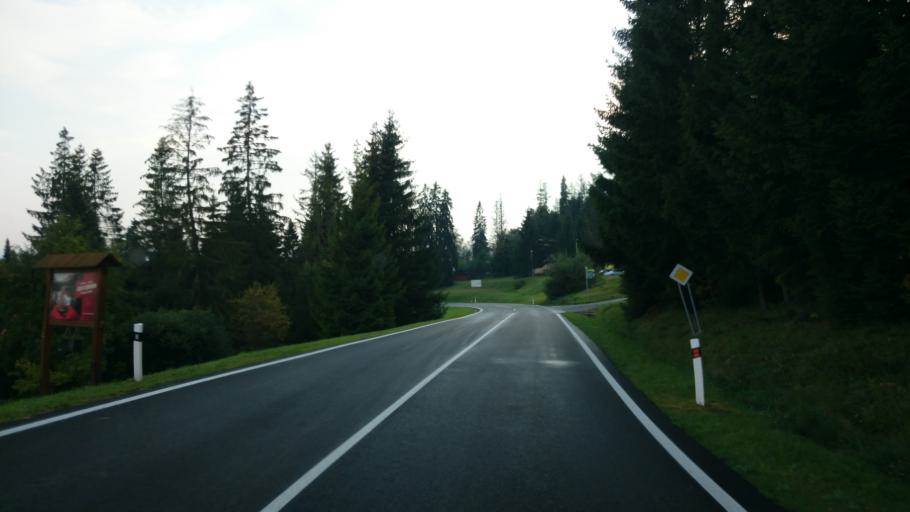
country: SK
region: Presovsky
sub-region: Okres Poprad
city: Strba
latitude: 49.0881
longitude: 20.0731
